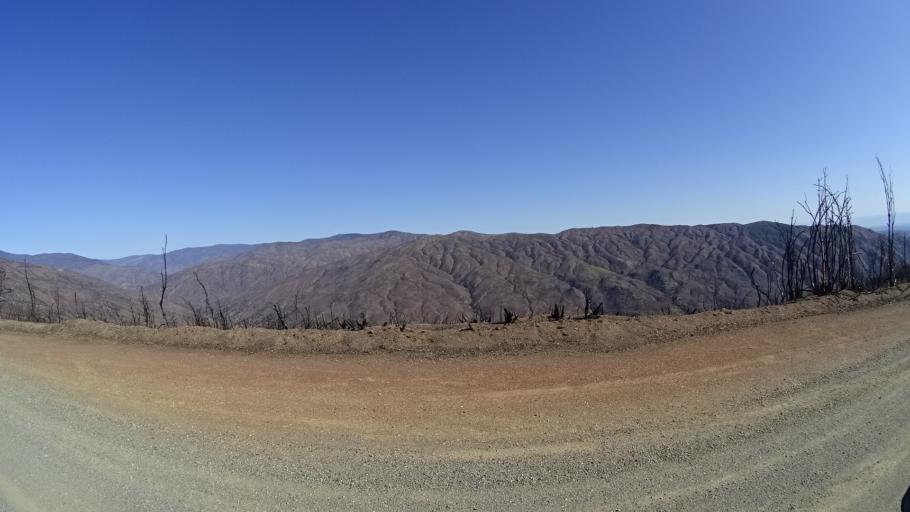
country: US
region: California
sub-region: Tehama County
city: Rancho Tehama Reserve
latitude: 39.6662
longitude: -122.6632
